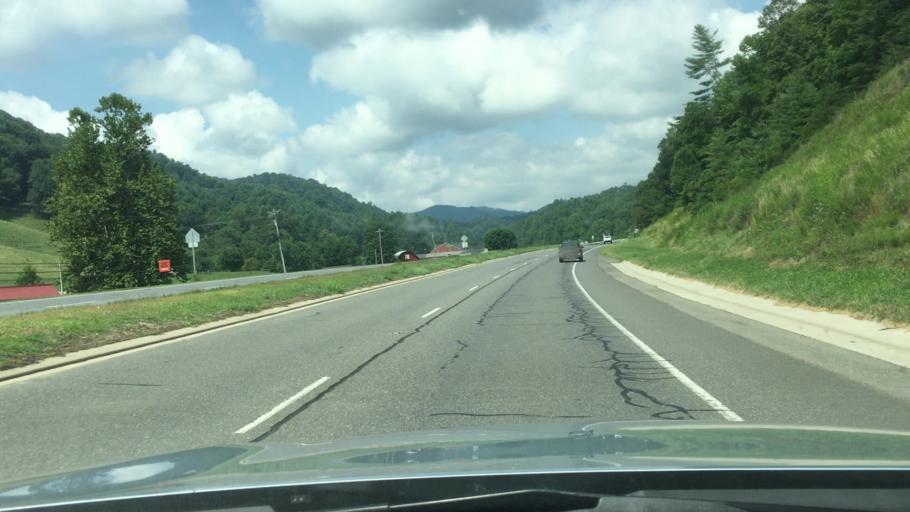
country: US
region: North Carolina
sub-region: Yancey County
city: Burnsville
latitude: 35.9137
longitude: -82.4245
